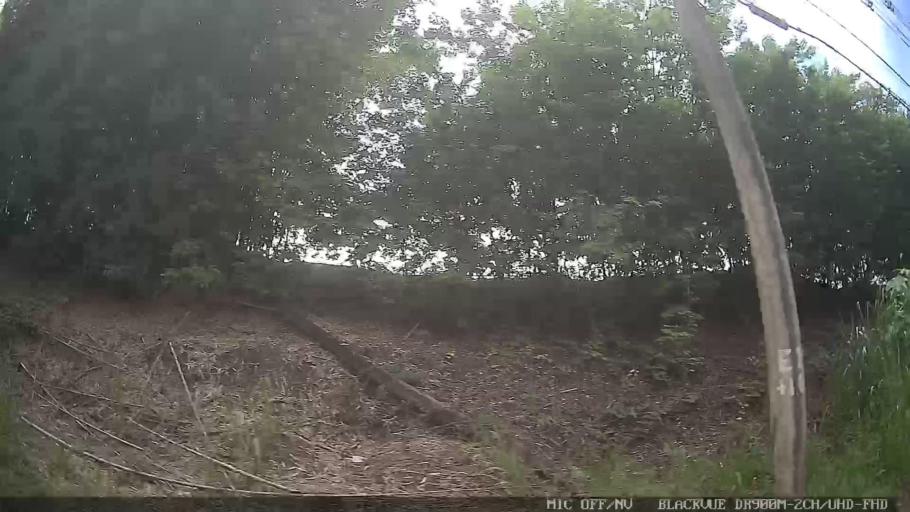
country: BR
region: Sao Paulo
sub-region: Santa Isabel
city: Santa Isabel
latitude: -23.4186
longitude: -46.2167
